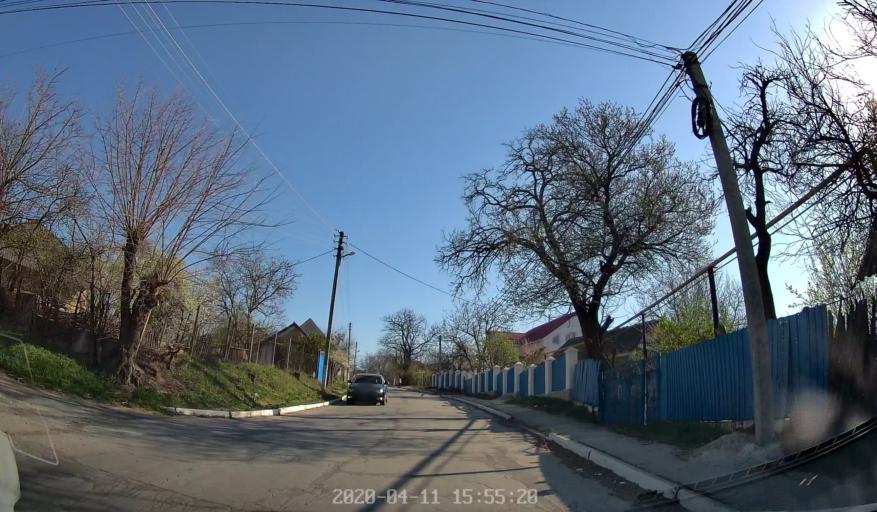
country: MD
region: Chisinau
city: Vadul lui Voda
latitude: 47.0964
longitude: 29.1772
